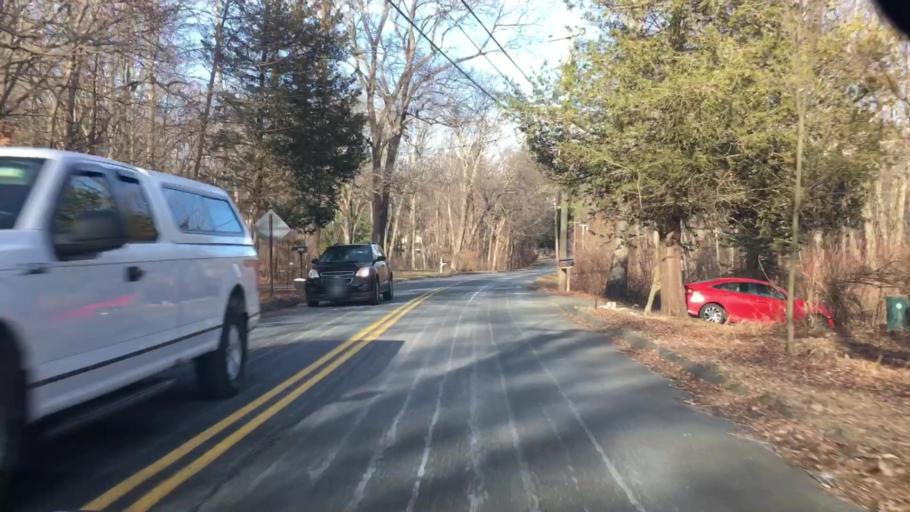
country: US
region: Connecticut
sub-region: New Haven County
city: Prospect
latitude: 41.5278
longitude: -72.9585
